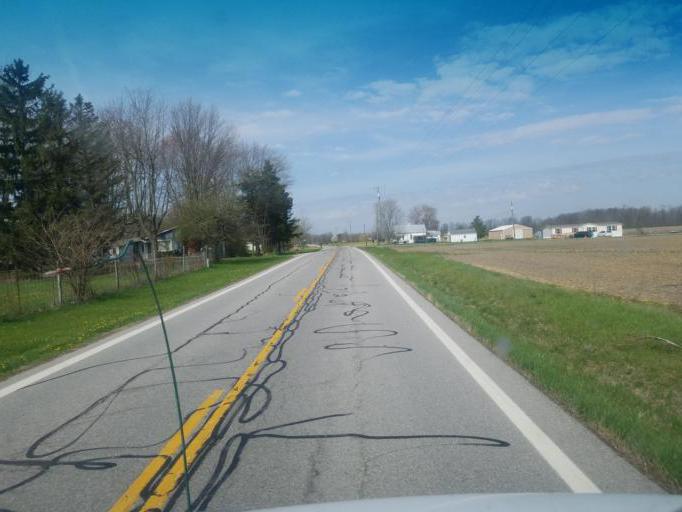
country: US
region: Ohio
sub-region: Union County
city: Richwood
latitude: 40.4826
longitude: -83.3915
